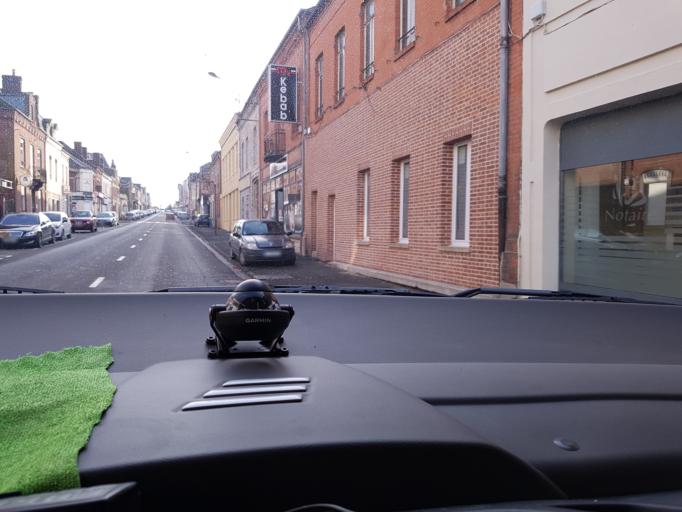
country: FR
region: Picardie
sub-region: Departement de l'Aisne
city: Hirson
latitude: 49.9218
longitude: 4.0832
